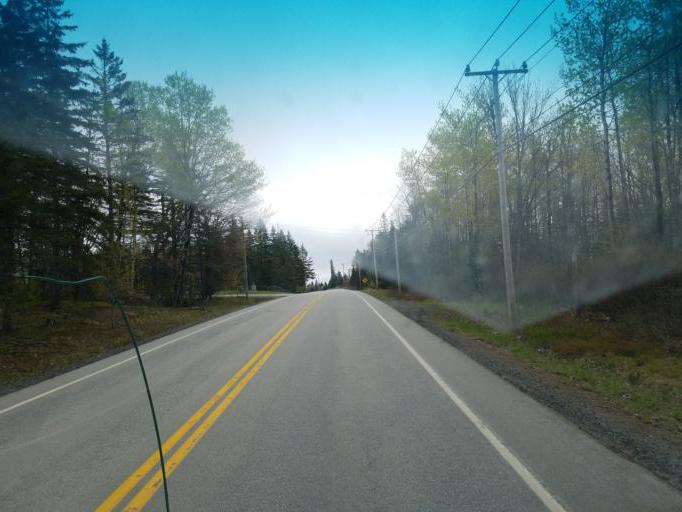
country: US
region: Maine
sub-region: Washington County
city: Eastport
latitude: 44.8010
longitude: -67.1279
